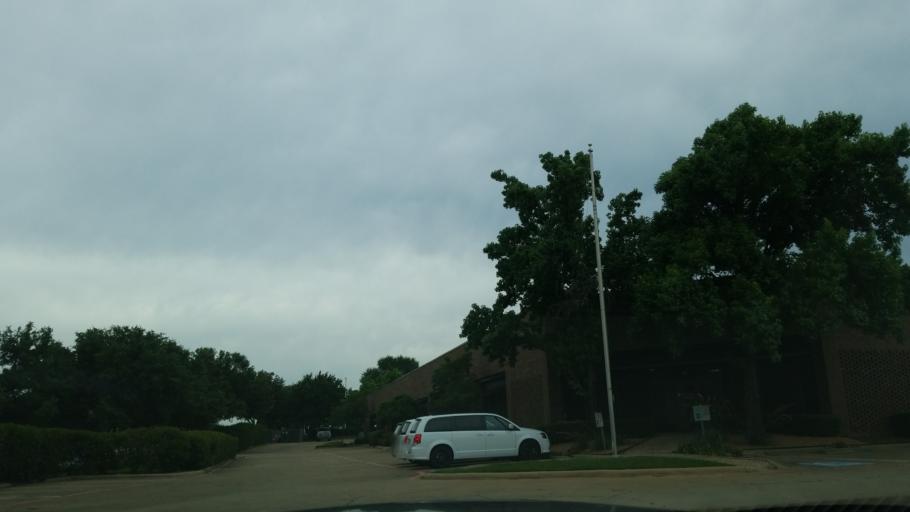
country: US
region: Texas
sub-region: Dallas County
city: Coppell
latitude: 32.8973
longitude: -96.9844
